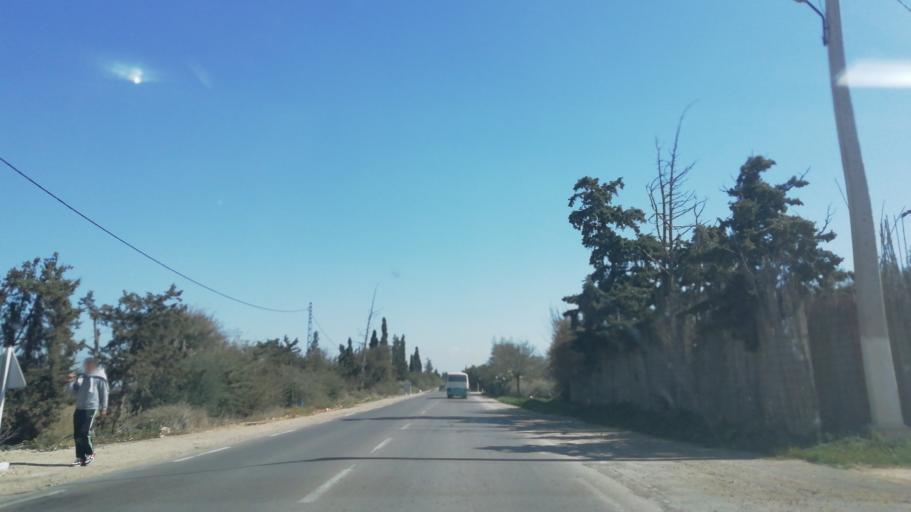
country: DZ
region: Mascara
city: Sig
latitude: 35.5705
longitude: -0.0396
